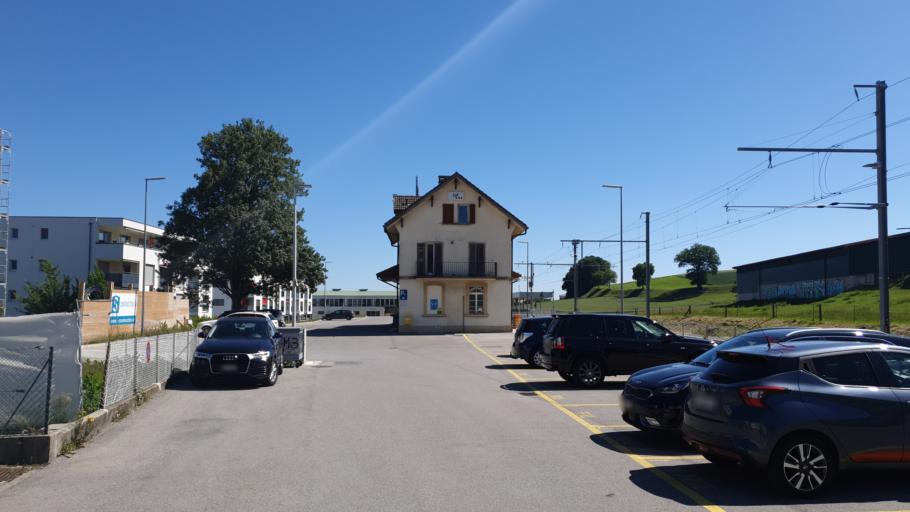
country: CH
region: Fribourg
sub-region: Sarine District
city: Belfaux
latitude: 46.8214
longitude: 7.1083
